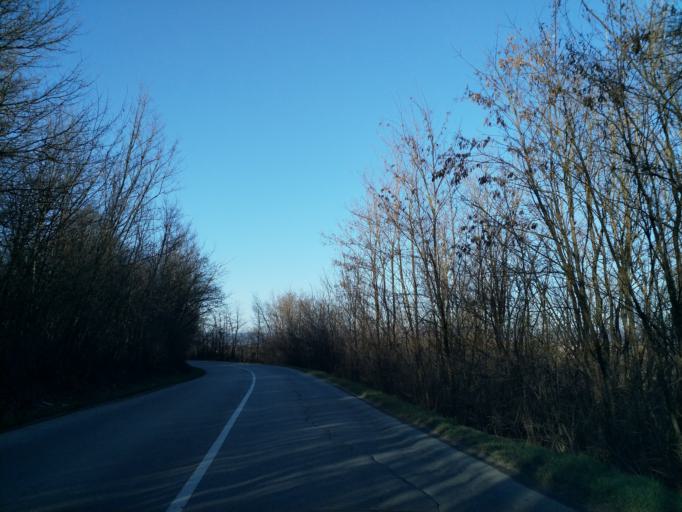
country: RS
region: Central Serbia
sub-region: Pomoravski Okrug
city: Paracin
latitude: 43.8727
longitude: 21.4708
